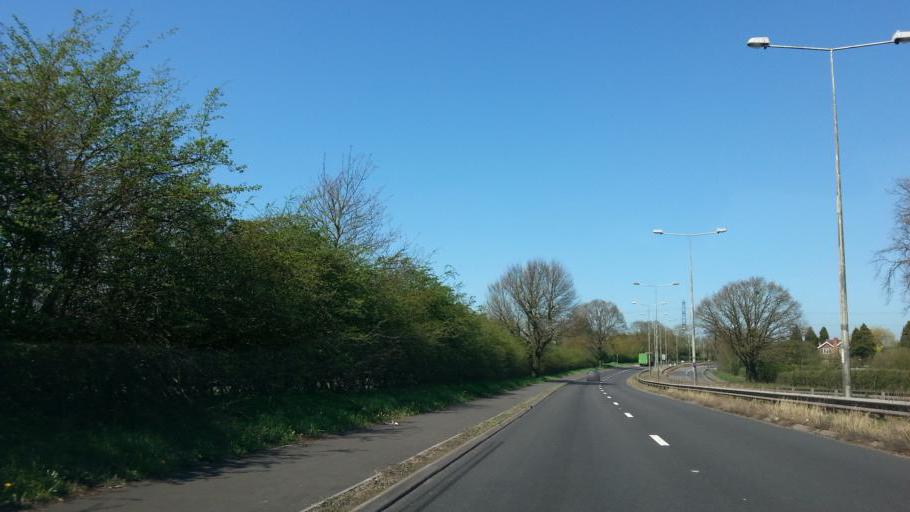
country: GB
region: England
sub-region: Staffordshire
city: Featherstone
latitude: 52.6600
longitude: -2.1307
